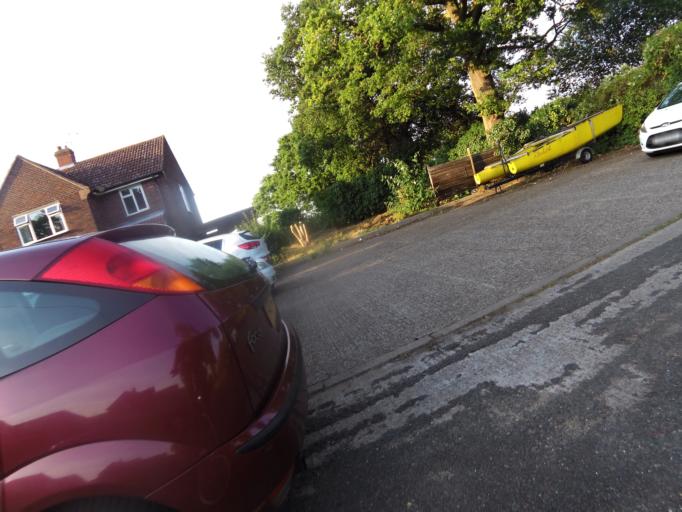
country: GB
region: England
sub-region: Suffolk
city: Ipswich
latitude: 52.0414
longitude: 1.1491
